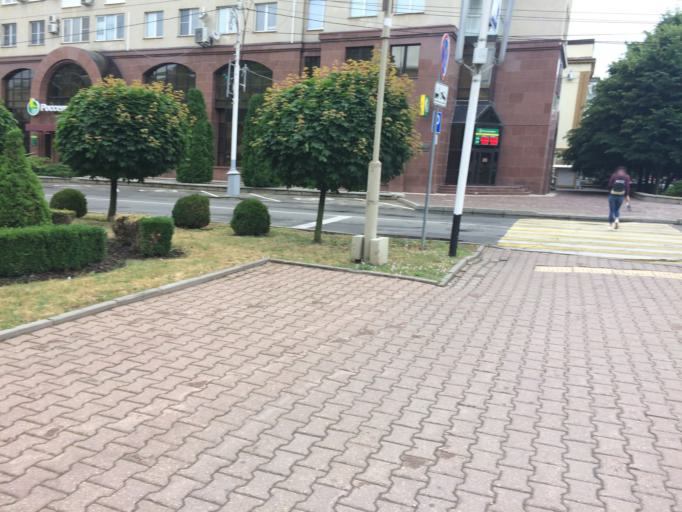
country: RU
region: Stavropol'skiy
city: Stavropol'
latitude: 45.0398
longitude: 41.9700
